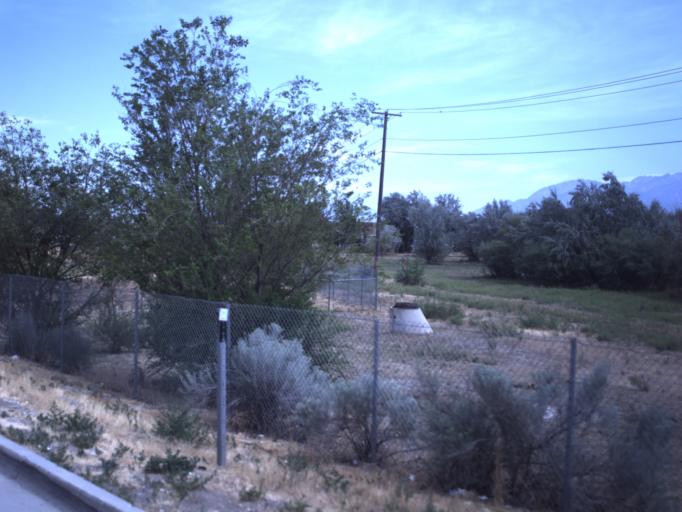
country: US
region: Utah
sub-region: Salt Lake County
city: Draper
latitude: 40.5028
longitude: -111.8855
